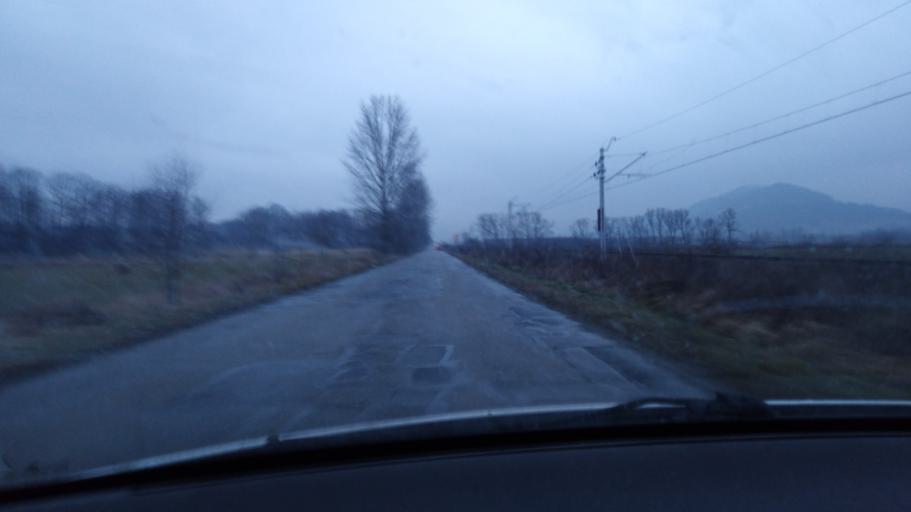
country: PL
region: Silesian Voivodeship
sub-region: Powiat zywiecki
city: Wieprz
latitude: 49.6406
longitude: 19.1587
